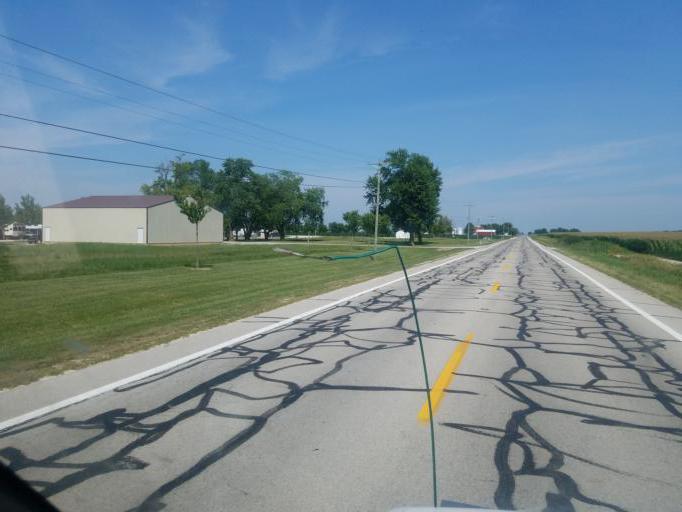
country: US
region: Ohio
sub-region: Auglaize County
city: Saint Marys
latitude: 40.4947
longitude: -84.4722
